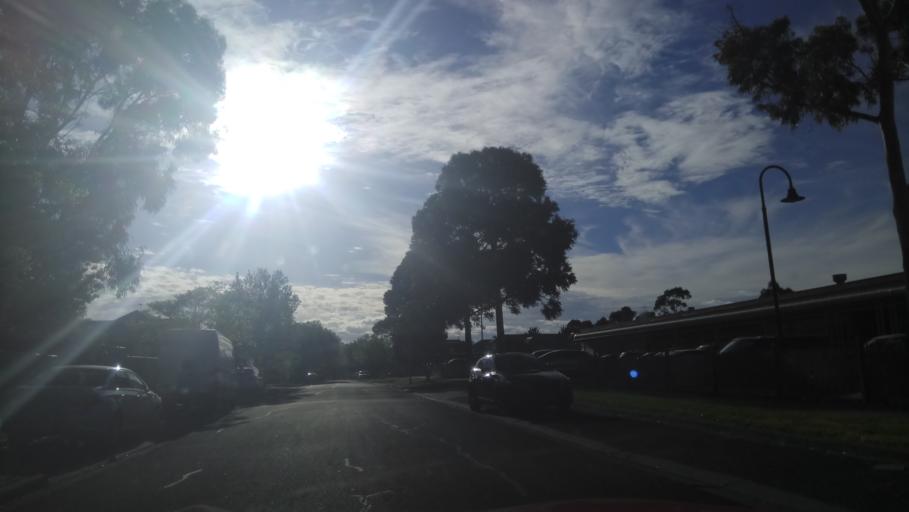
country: AU
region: Victoria
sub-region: Hobsons Bay
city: Williamstown North
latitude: -37.8582
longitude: 144.8828
